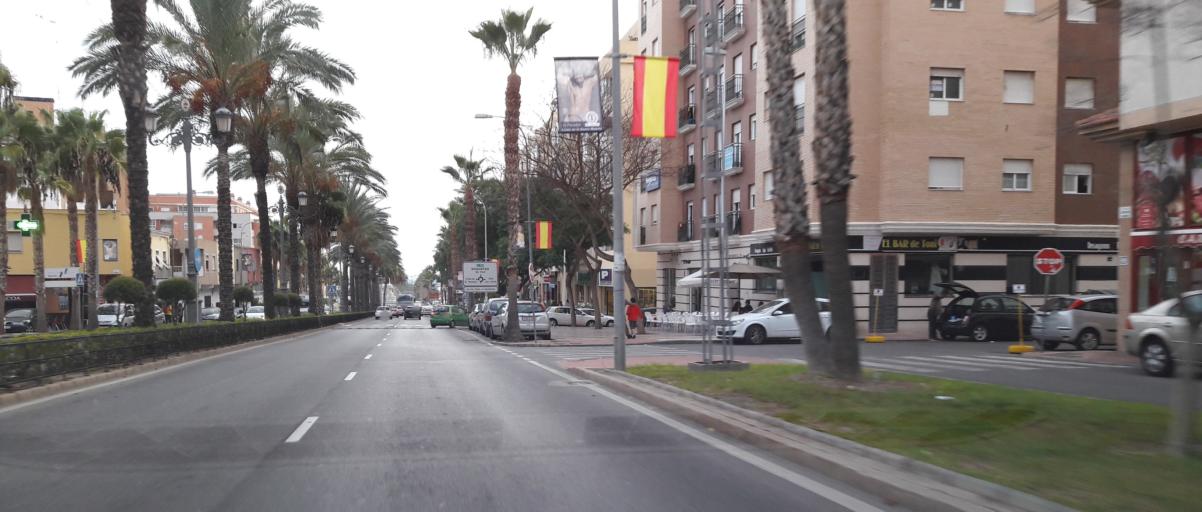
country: ES
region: Andalusia
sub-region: Provincia de Almeria
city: Aguadulce
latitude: 36.8052
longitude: -2.5992
